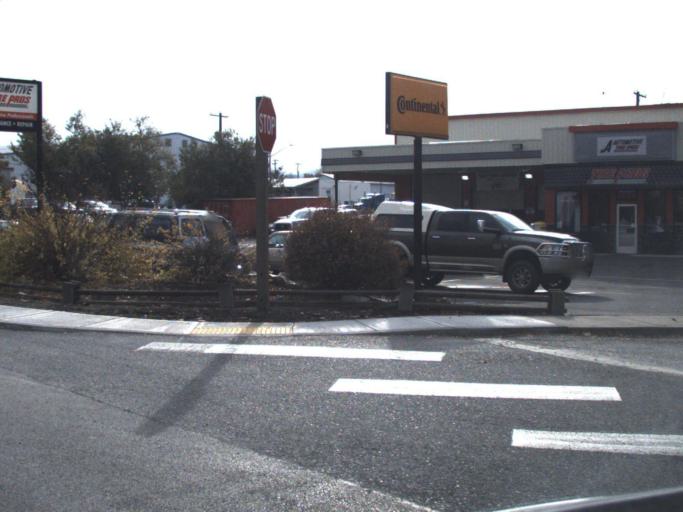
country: US
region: Washington
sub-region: Stevens County
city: Colville
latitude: 48.5487
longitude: -117.9094
